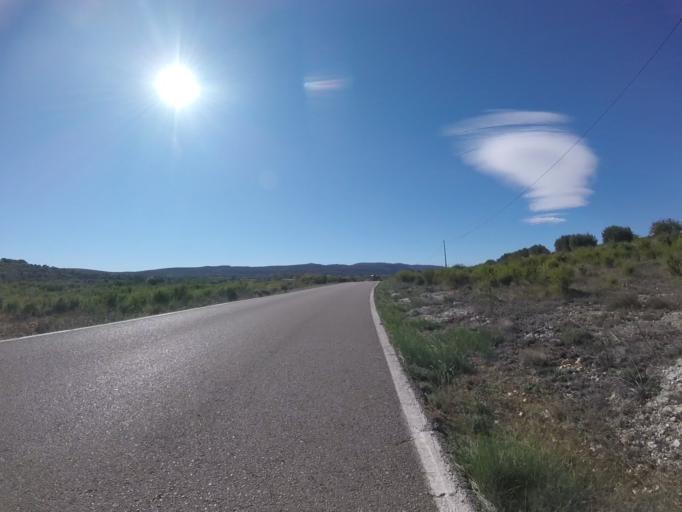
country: ES
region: Valencia
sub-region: Provincia de Castello
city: Albocasser
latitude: 40.3738
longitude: 0.0199
